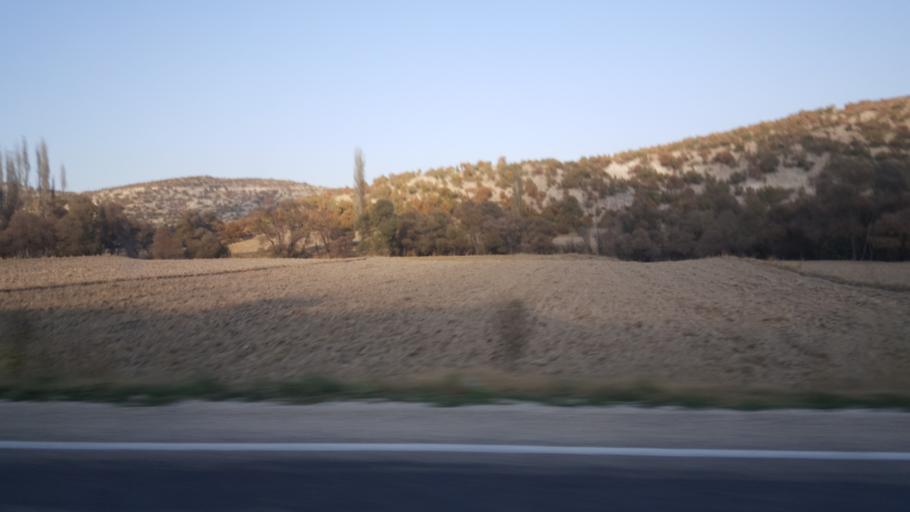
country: TR
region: Eskisehir
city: Kirka
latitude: 39.3609
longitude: 30.5903
